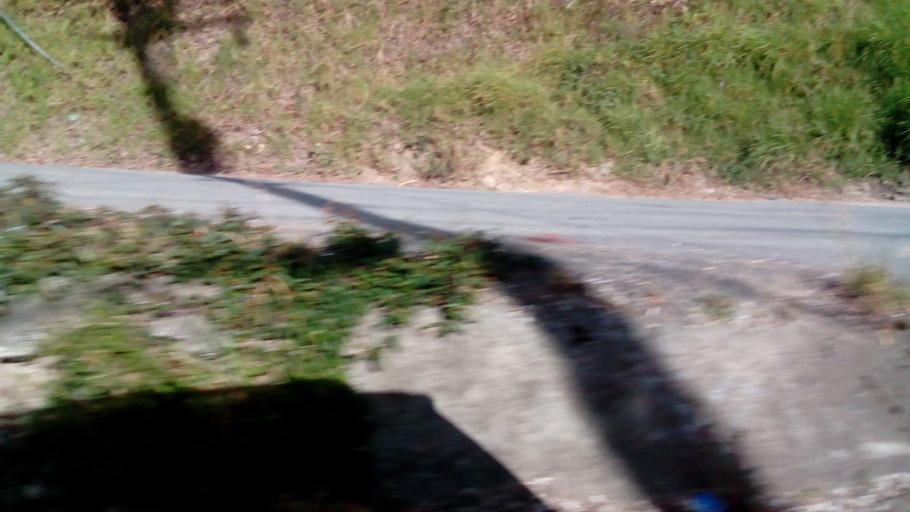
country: TW
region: Taiwan
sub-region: Hualien
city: Hualian
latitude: 24.3281
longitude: 121.3078
